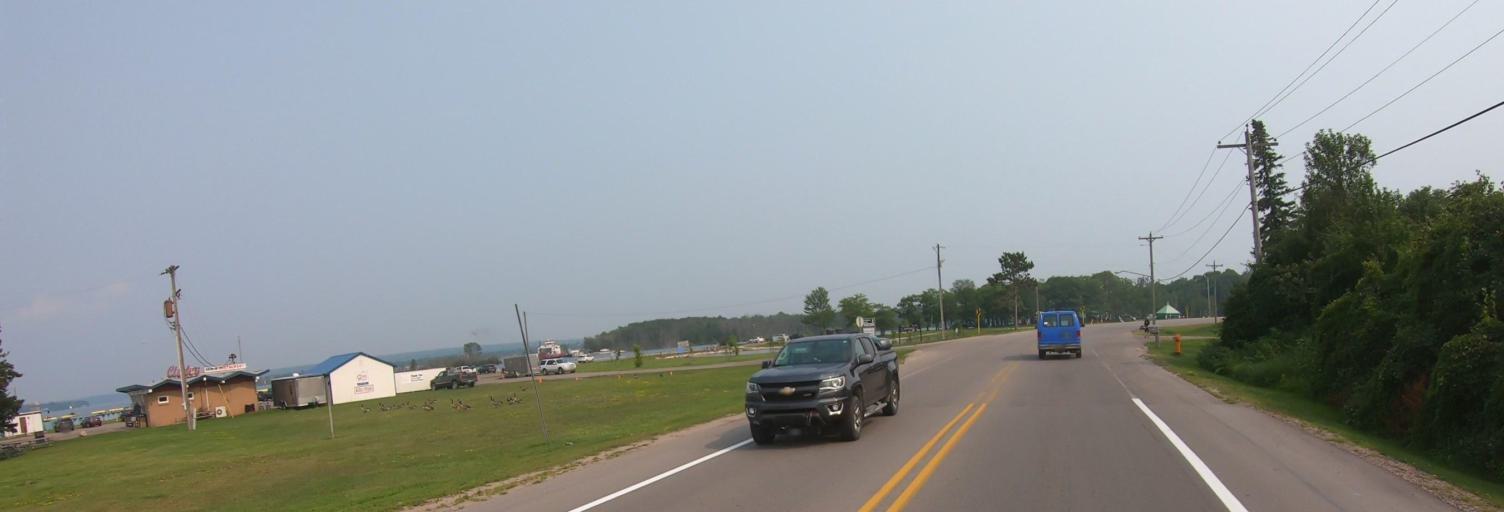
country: US
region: Michigan
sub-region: Chippewa County
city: Sault Ste. Marie
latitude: 46.4855
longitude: -84.3034
